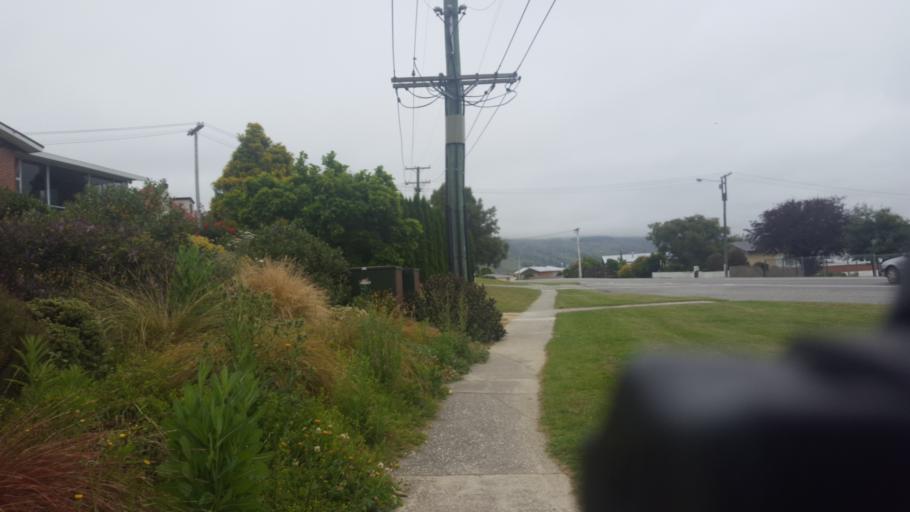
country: NZ
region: Otago
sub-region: Queenstown-Lakes District
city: Kingston
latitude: -45.5381
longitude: 169.3104
